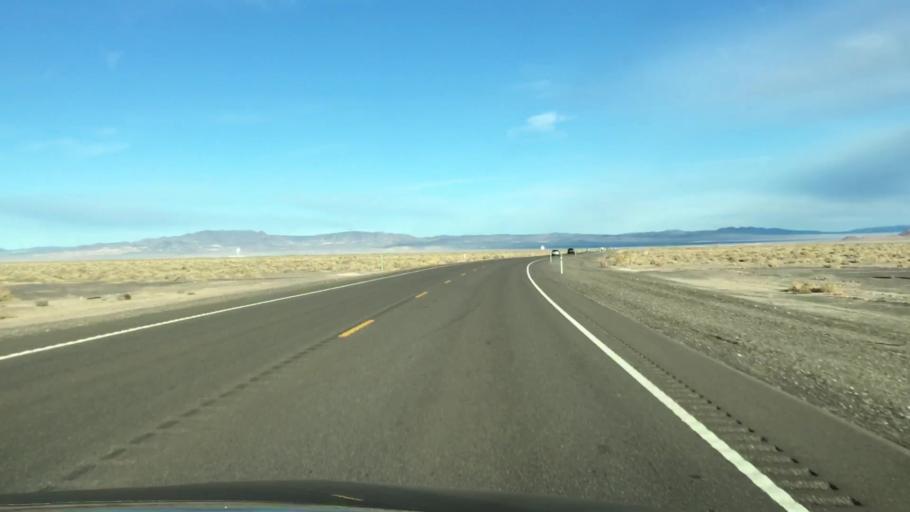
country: US
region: Nevada
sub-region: Nye County
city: Tonopah
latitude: 38.1275
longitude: -117.5750
